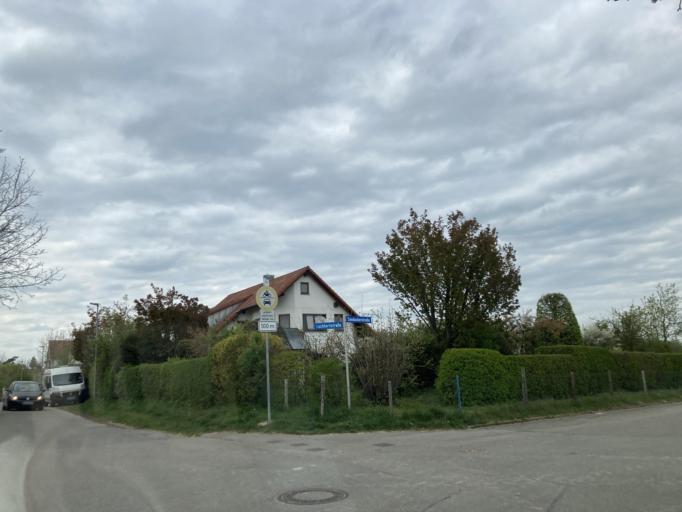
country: DE
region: Baden-Wuerttemberg
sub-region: Tuebingen Region
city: Kusterdingen
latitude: 48.5035
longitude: 9.1288
